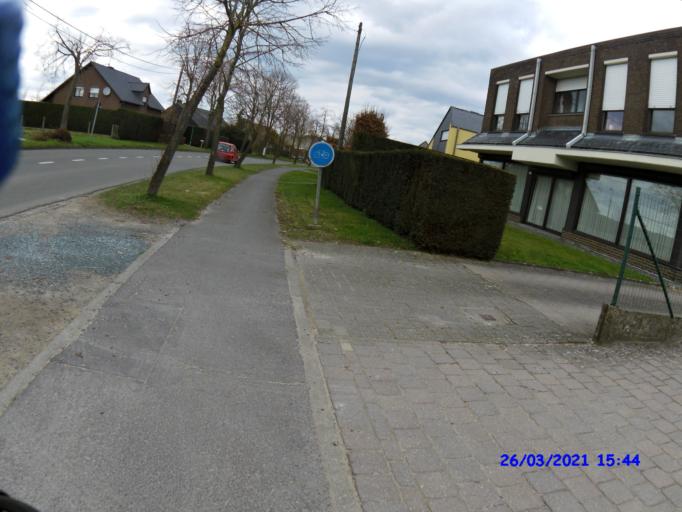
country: BE
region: Flanders
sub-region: Provincie Oost-Vlaanderen
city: Buggenhout
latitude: 51.0126
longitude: 4.1784
